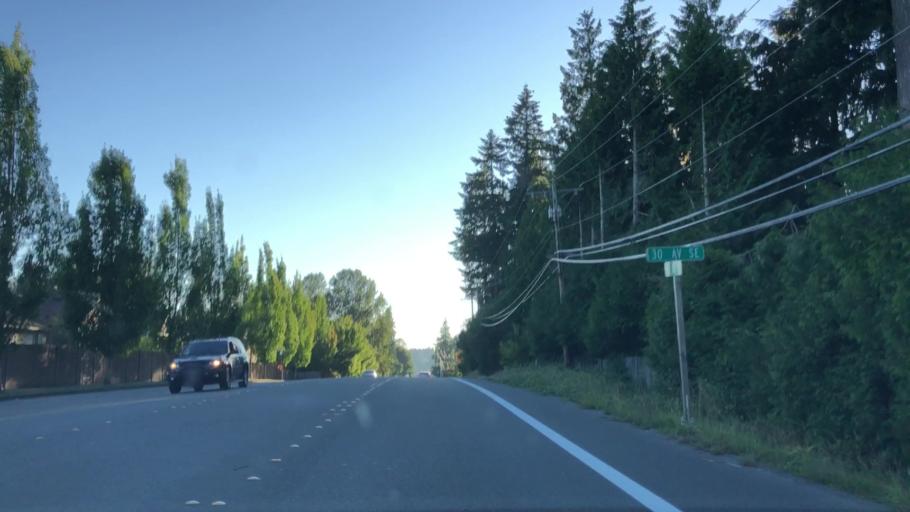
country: US
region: Washington
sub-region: Snohomish County
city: North Creek
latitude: 47.8346
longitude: -122.1921
